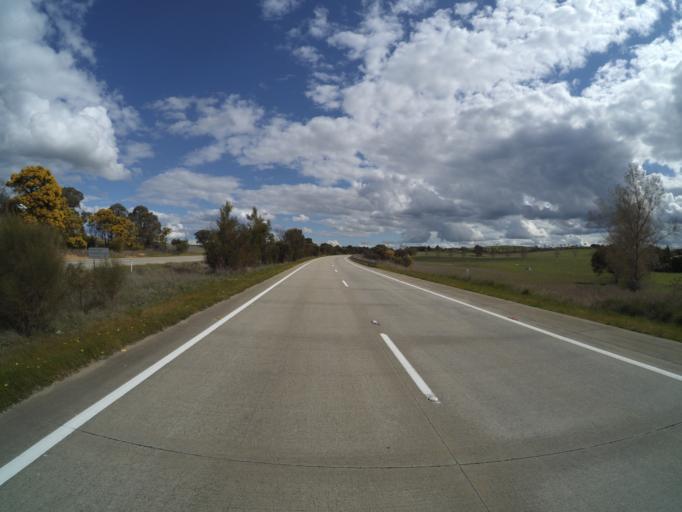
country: AU
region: New South Wales
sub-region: Yass Valley
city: Murrumbateman
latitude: -34.7900
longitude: 149.1739
